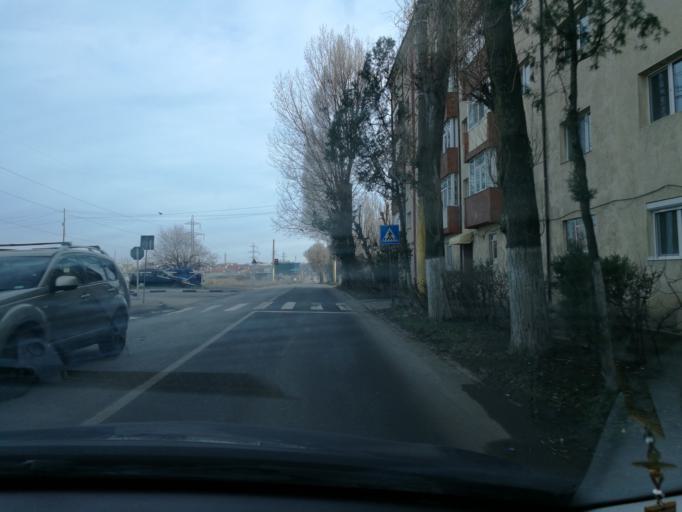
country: RO
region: Constanta
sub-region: Municipiul Constanta
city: Constanta
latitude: 44.1915
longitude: 28.6056
